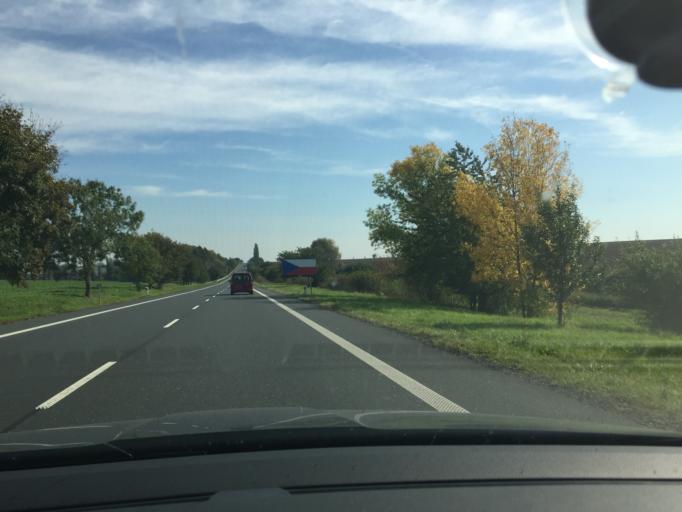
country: CZ
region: Central Bohemia
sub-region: Okres Kolin
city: Kourim
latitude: 50.0480
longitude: 14.9781
